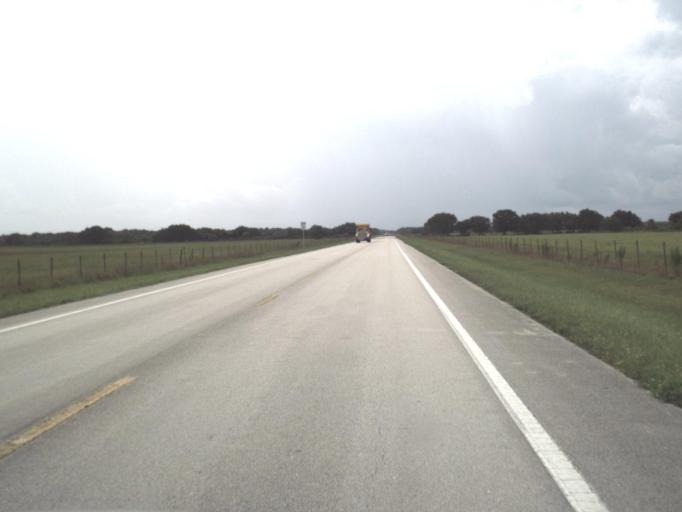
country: US
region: Florida
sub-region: Sarasota County
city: Warm Mineral Springs
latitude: 27.1934
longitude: -82.1624
